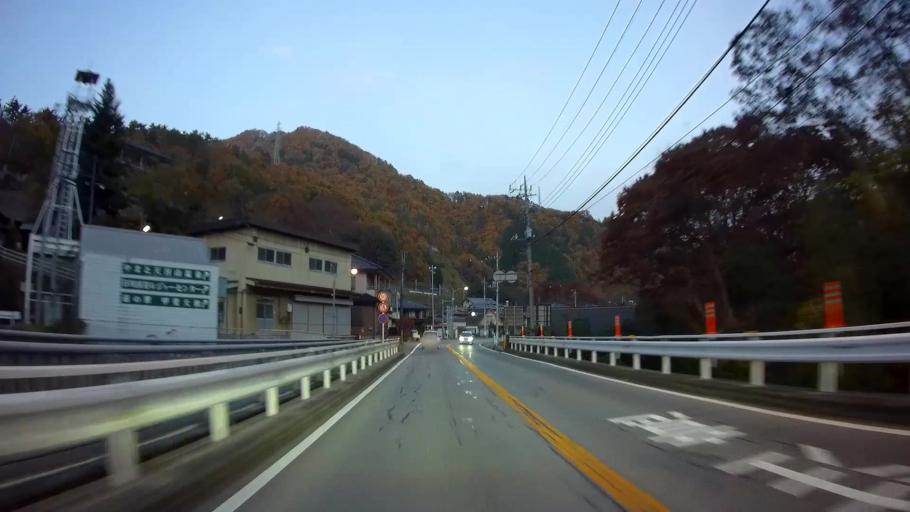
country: JP
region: Yamanashi
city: Enzan
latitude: 35.6436
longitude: 138.7676
